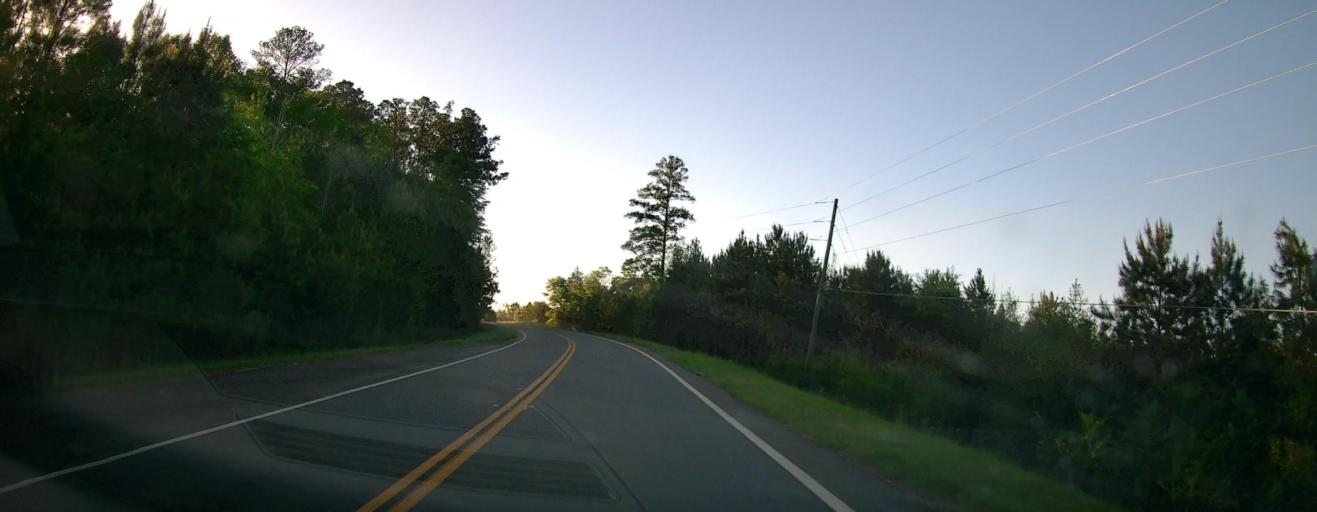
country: US
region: Georgia
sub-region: Macon County
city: Oglethorpe
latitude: 32.3116
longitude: -84.1629
